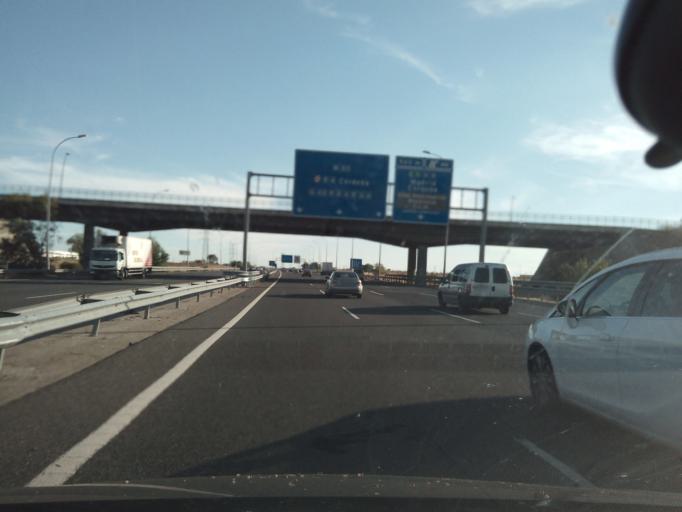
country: ES
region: Madrid
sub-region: Provincia de Madrid
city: Pinto
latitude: 40.2889
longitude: -3.6780
